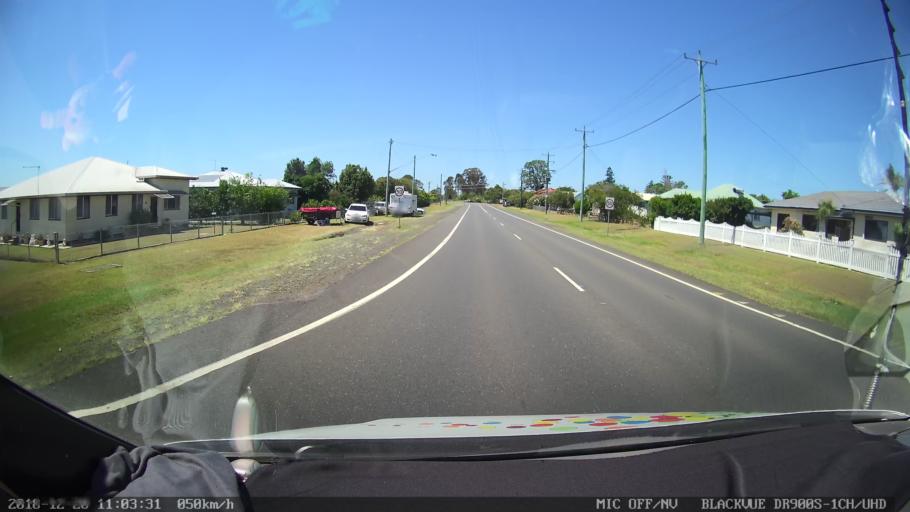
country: AU
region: New South Wales
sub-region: Richmond Valley
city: Casino
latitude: -28.8776
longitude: 153.0430
